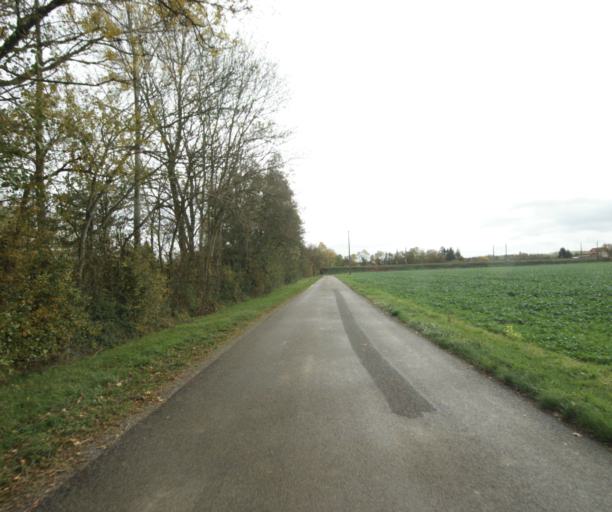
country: FR
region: Rhone-Alpes
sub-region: Departement de l'Ain
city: Pont-de-Vaux
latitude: 46.4709
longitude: 4.8924
